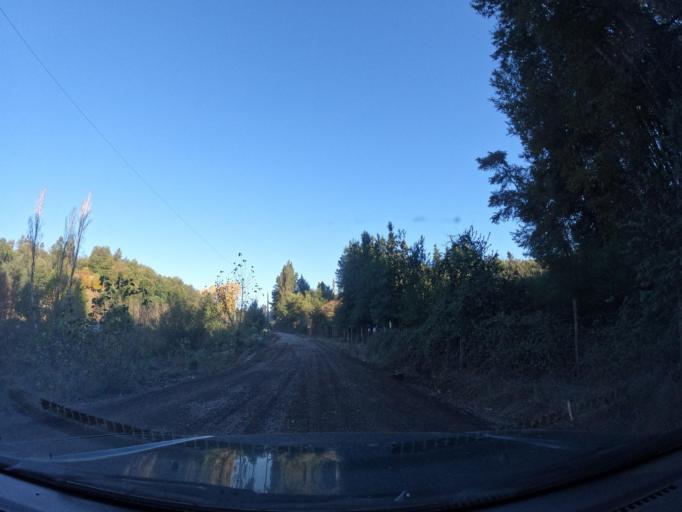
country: CL
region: Biobio
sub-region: Provincia de Concepcion
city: Chiguayante
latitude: -37.0281
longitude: -72.8848
